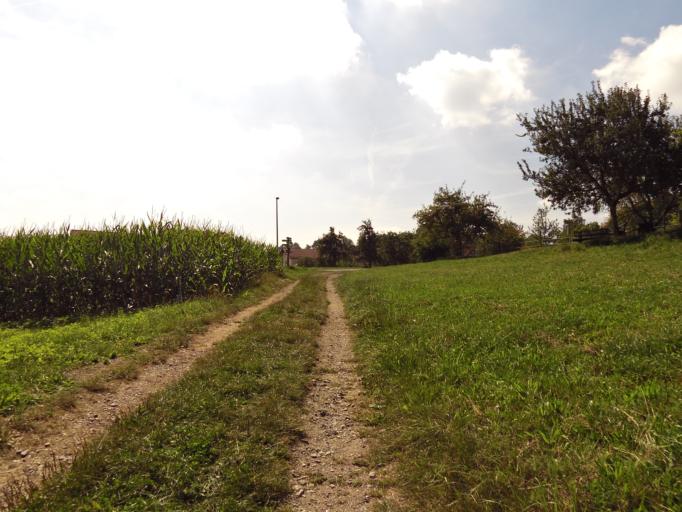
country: DE
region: Hesse
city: Lutzelbach
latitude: 49.7235
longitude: 8.8008
